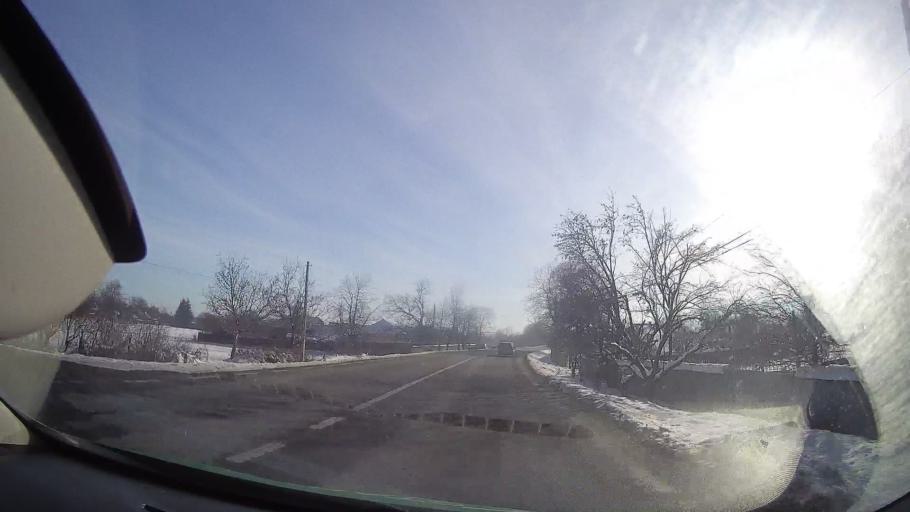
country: RO
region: Neamt
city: Bodesti
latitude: 47.0510
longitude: 26.4028
